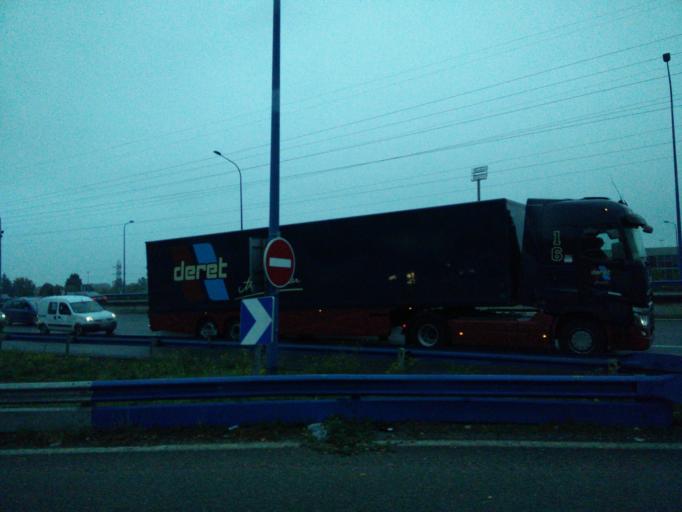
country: FR
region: Midi-Pyrenees
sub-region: Departement de la Haute-Garonne
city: Blagnac
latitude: 43.6221
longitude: 1.4181
